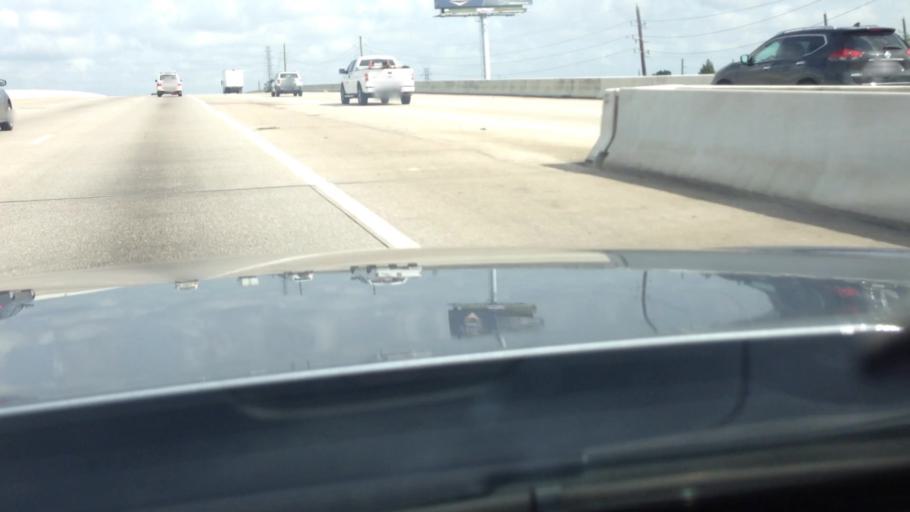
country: US
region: Texas
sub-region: Harris County
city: Hudson
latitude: 29.9433
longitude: -95.5244
